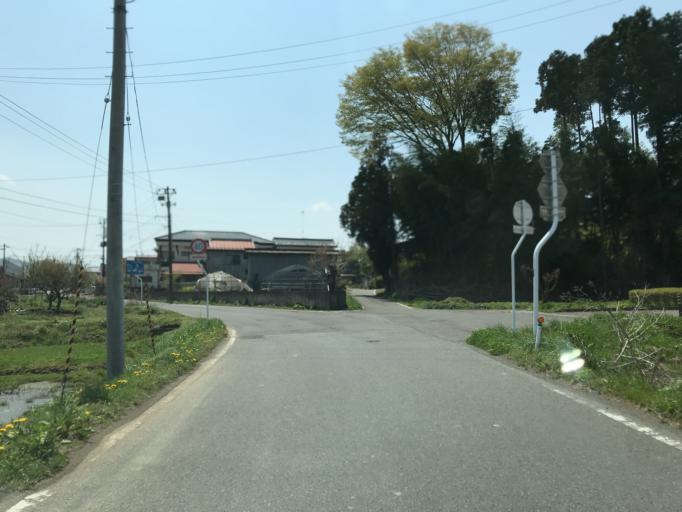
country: JP
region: Fukushima
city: Ishikawa
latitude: 37.0854
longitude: 140.4167
